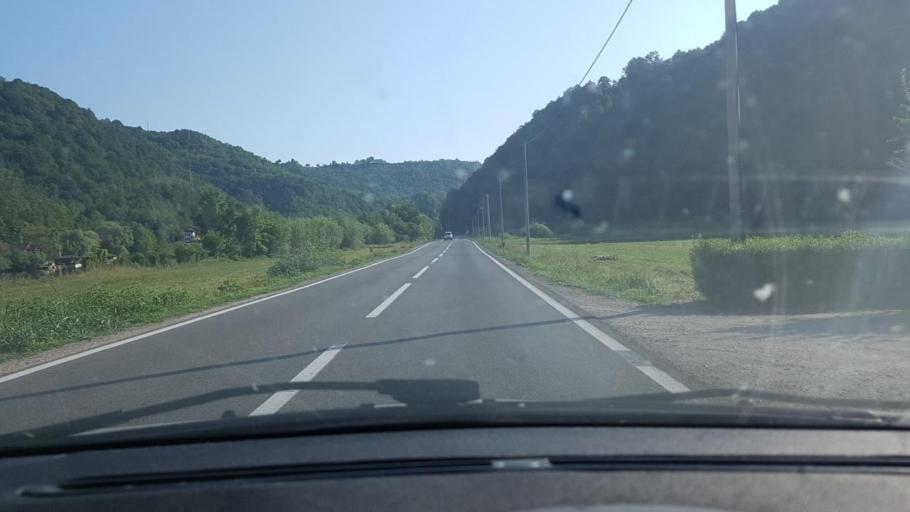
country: BA
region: Federation of Bosnia and Herzegovina
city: Ostrozac
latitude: 44.8769
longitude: 15.8915
